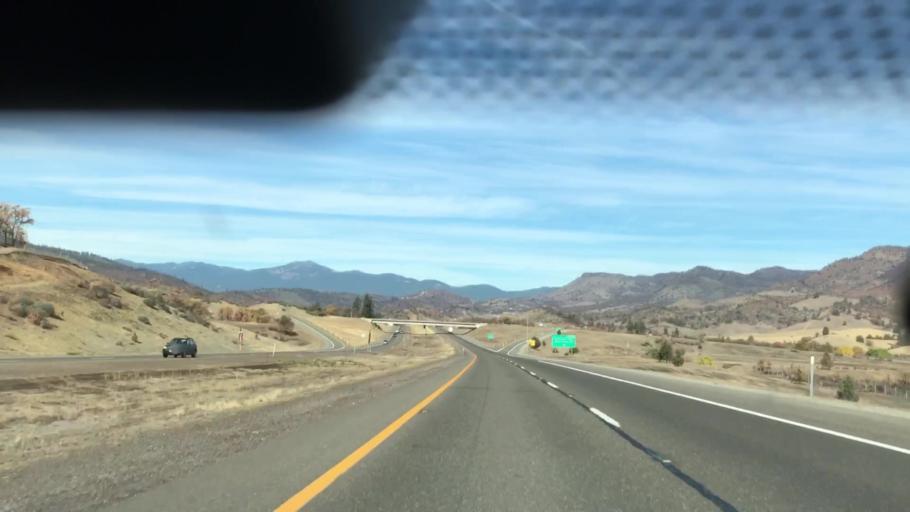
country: US
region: California
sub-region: Siskiyou County
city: Yreka
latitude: 41.9150
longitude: -122.5714
